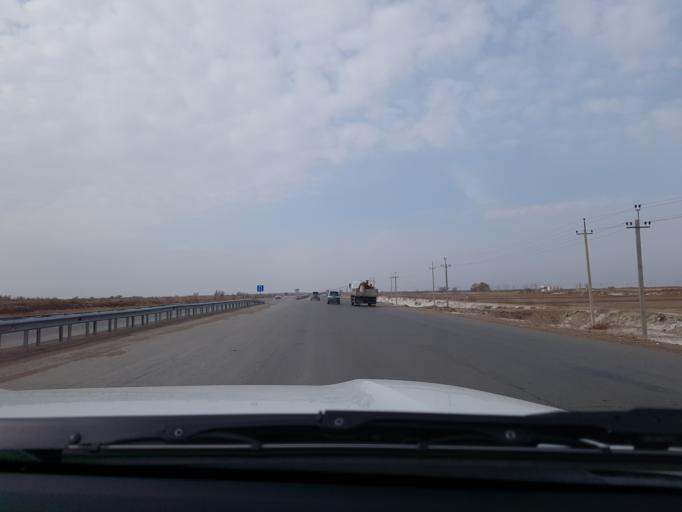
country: TM
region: Dasoguz
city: Yylanly
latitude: 41.7619
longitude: 59.4212
